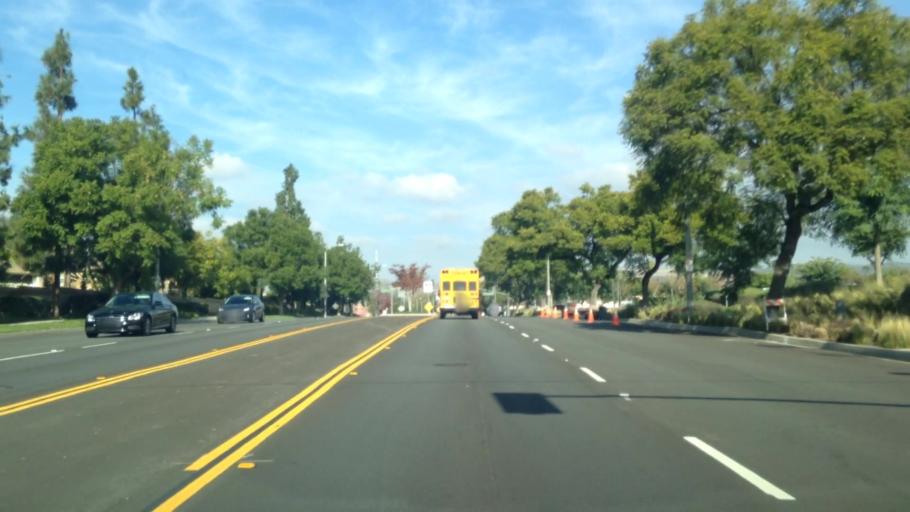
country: US
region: California
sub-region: Orange County
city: Yorba Linda
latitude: 33.8974
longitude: -117.8419
